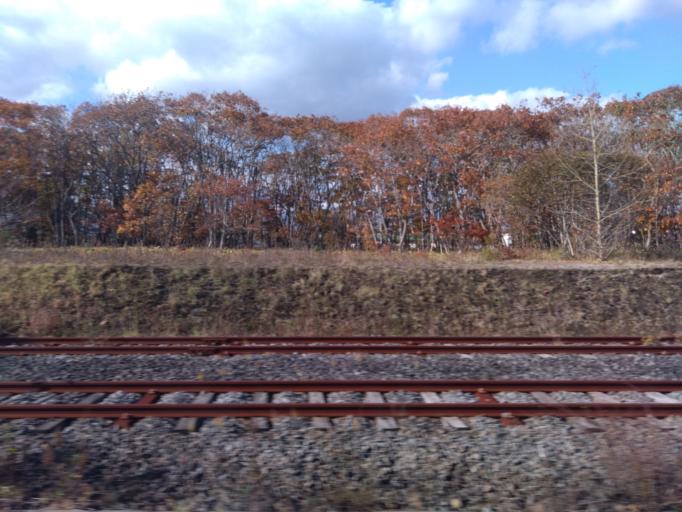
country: JP
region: Hokkaido
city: Shiraoi
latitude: 42.5178
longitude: 141.3002
